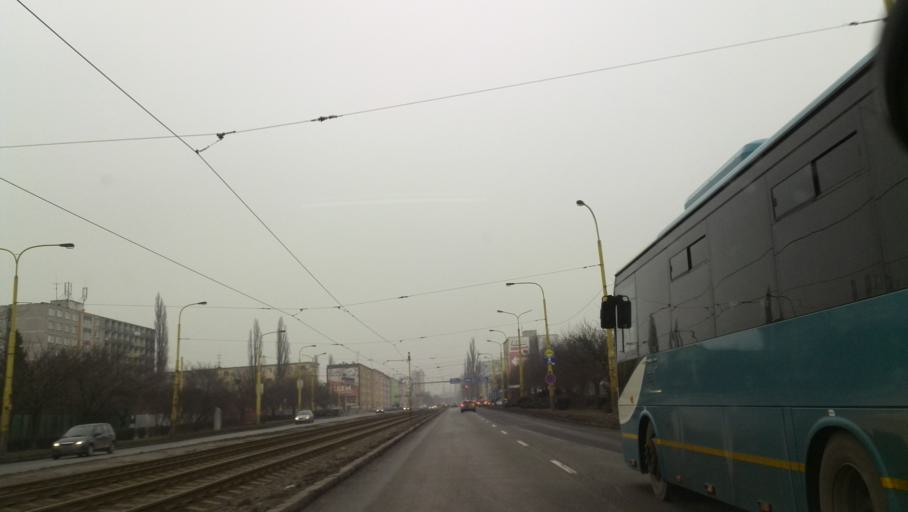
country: SK
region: Kosicky
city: Kosice
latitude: 48.7021
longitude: 21.2629
